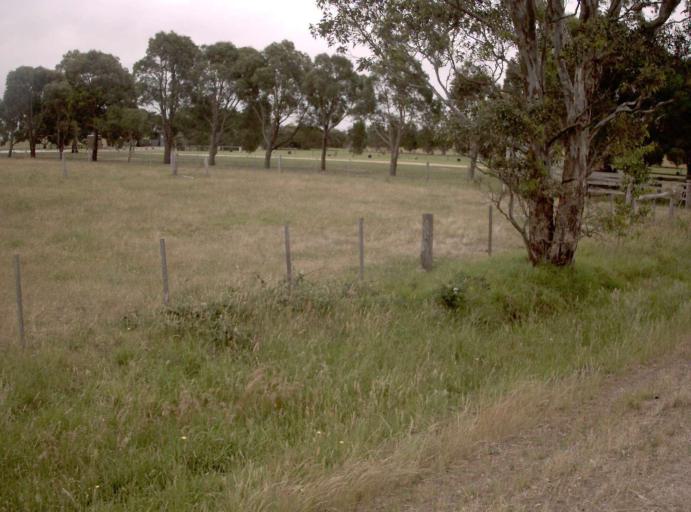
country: AU
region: Victoria
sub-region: East Gippsland
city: Bairnsdale
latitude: -37.8233
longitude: 147.4349
